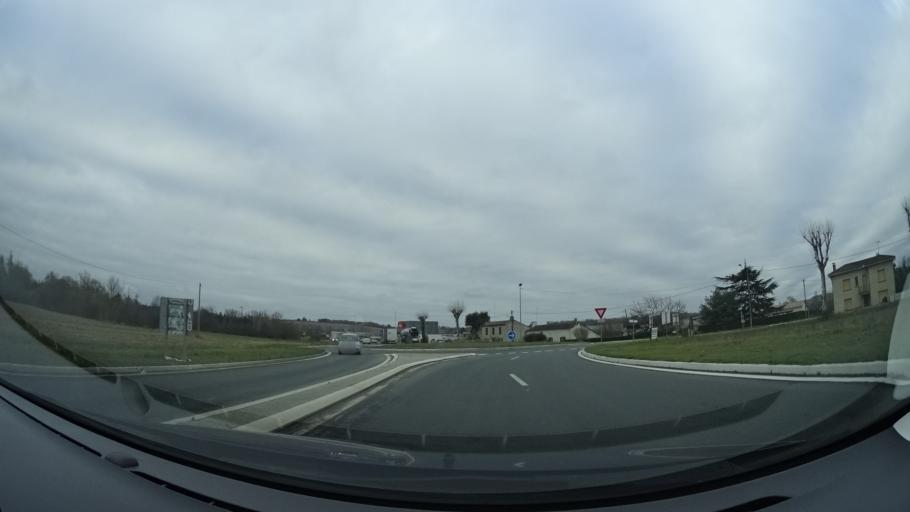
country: FR
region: Aquitaine
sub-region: Departement du Lot-et-Garonne
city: Damazan
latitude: 44.2875
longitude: 0.2725
